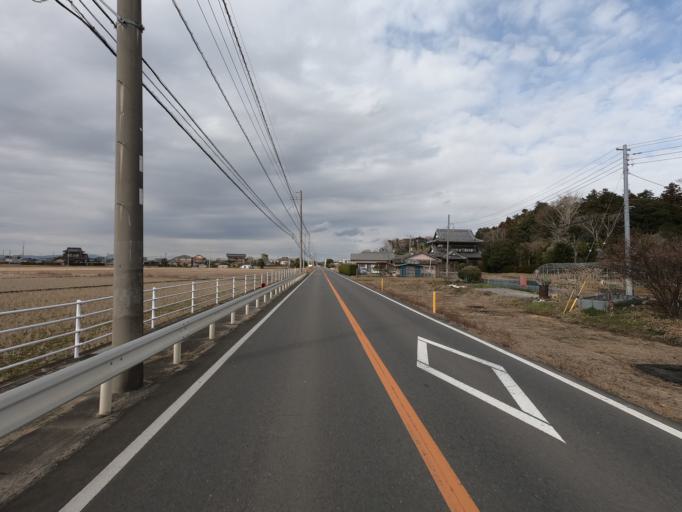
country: JP
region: Ibaraki
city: Inashiki
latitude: 36.0794
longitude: 140.4255
